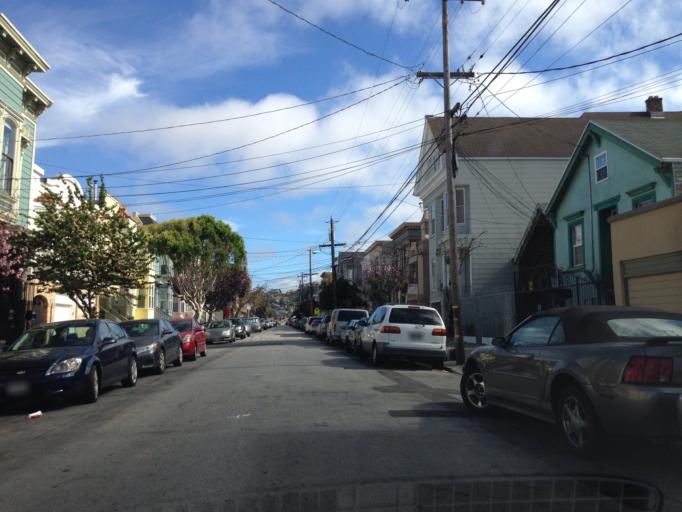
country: US
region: California
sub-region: San Francisco County
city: San Francisco
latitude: 37.7542
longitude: -122.4111
